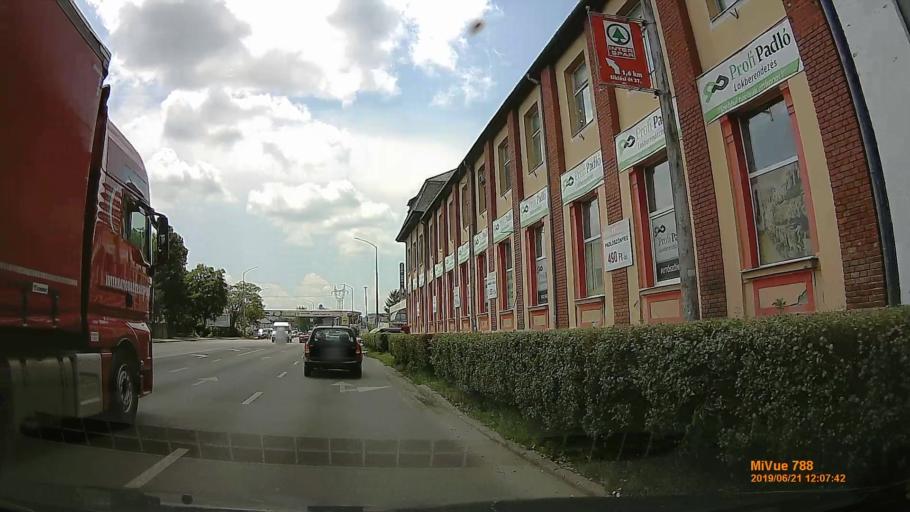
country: HU
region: Baranya
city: Pecs
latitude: 46.0627
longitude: 18.2308
